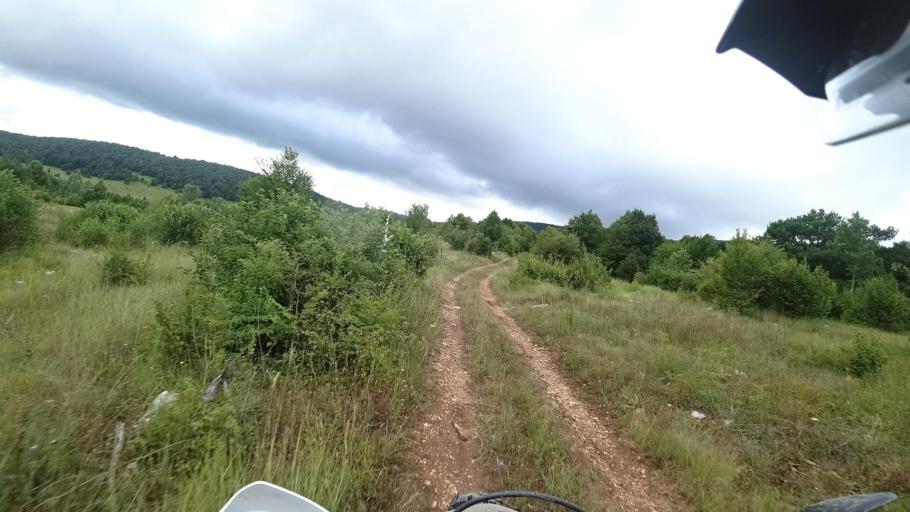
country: HR
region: Licko-Senjska
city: Jezerce
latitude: 44.7627
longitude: 15.4872
